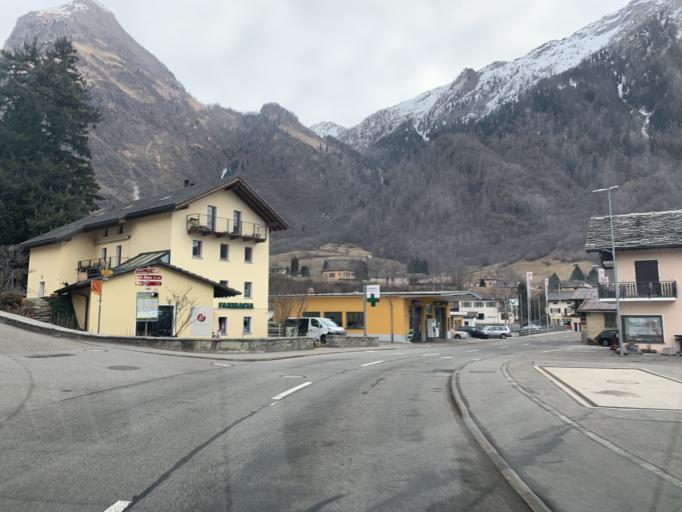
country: CH
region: Ticino
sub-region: Blenio District
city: Acquarossa
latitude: 46.5297
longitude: 8.9366
